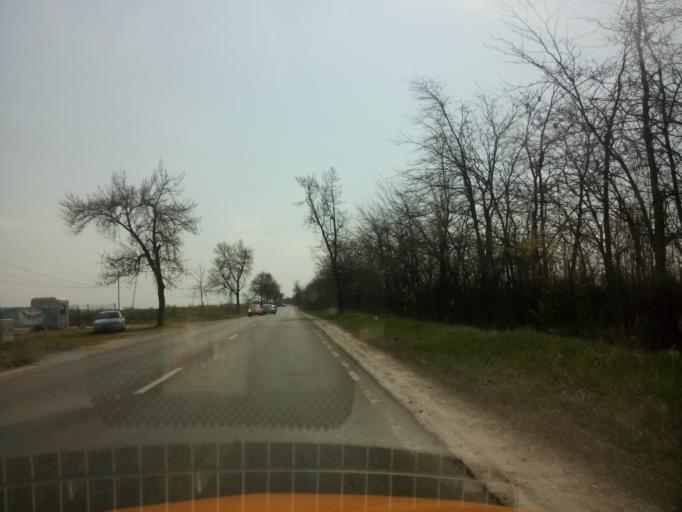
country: RO
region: Ilfov
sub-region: Comuna Glina
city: Glina
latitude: 44.3233
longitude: 26.2645
